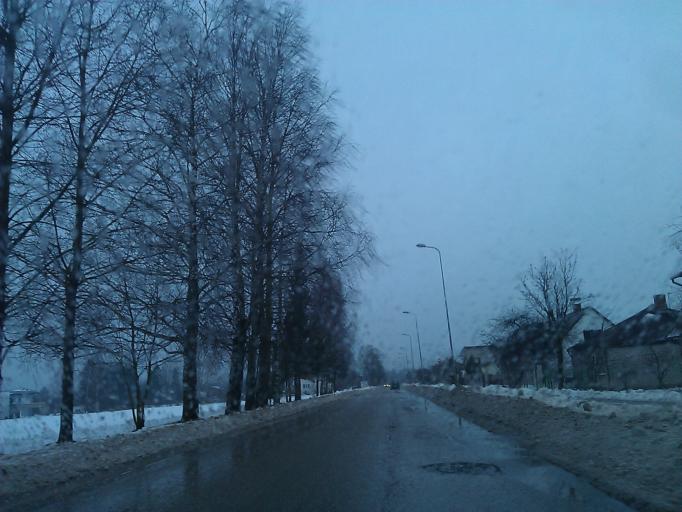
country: LV
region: Cesu Rajons
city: Cesis
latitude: 57.3020
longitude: 25.2942
